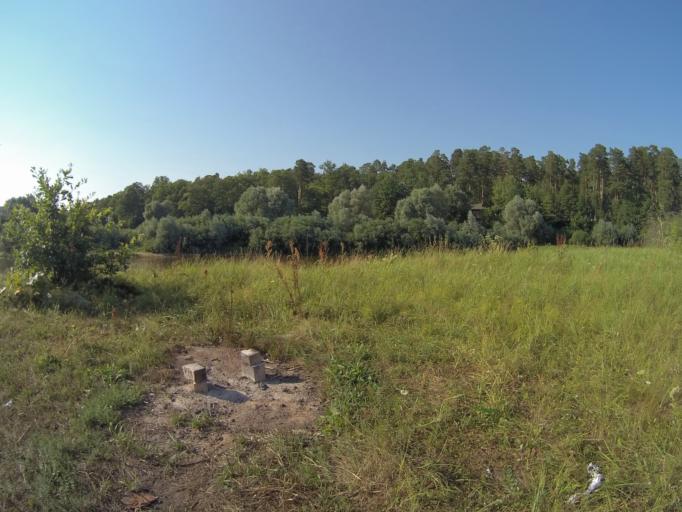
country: RU
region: Vladimir
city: Vorsha
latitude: 56.0402
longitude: 40.2037
